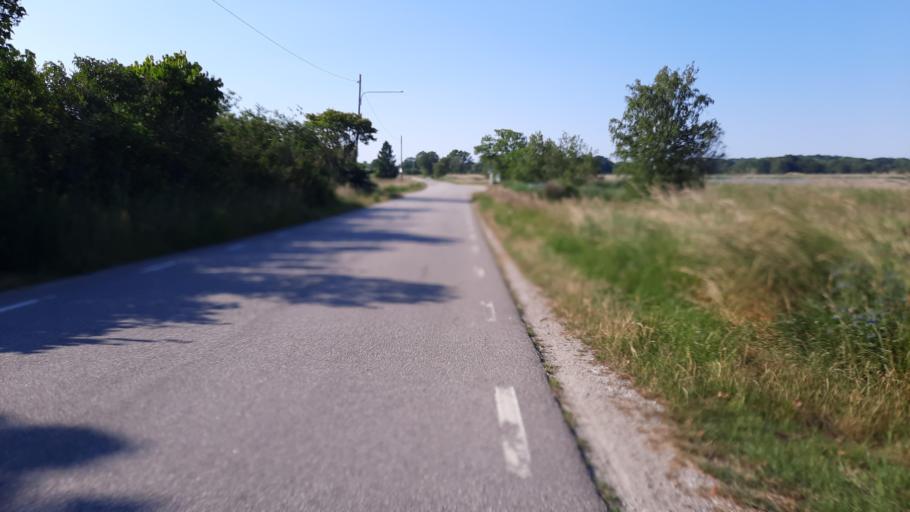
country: SE
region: Blekinge
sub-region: Karlskrona Kommun
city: Sturko
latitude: 56.1020
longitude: 15.6909
